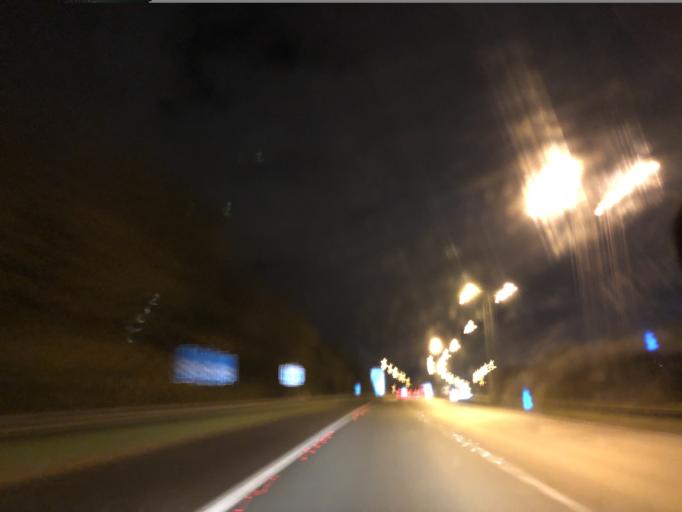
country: GB
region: England
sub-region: Kirklees
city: Cleckheaton
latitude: 53.7509
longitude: -1.7399
